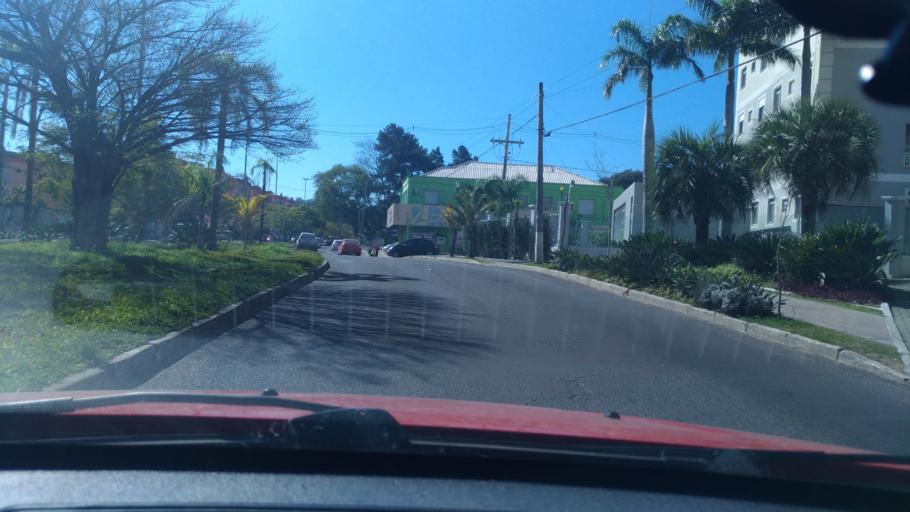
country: BR
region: Rio Grande do Sul
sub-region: Cachoeirinha
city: Cachoeirinha
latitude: -30.0405
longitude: -51.1293
